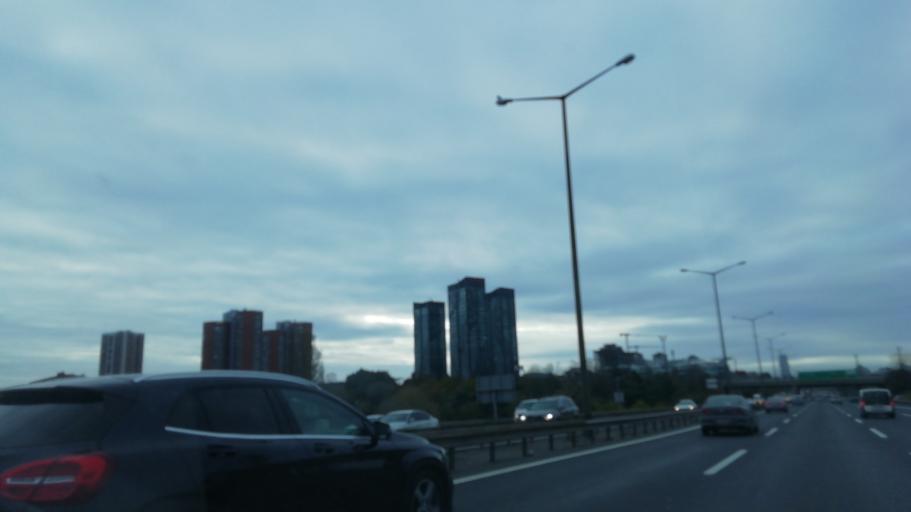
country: TR
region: Istanbul
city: Umraniye
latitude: 41.0329
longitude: 29.1209
